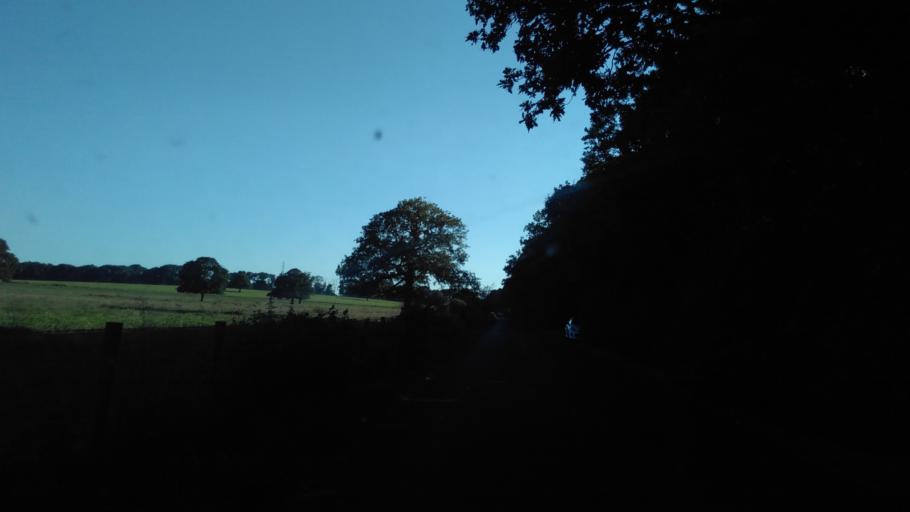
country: GB
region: England
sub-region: Kent
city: Dunkirk
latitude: 51.3086
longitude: 0.9953
